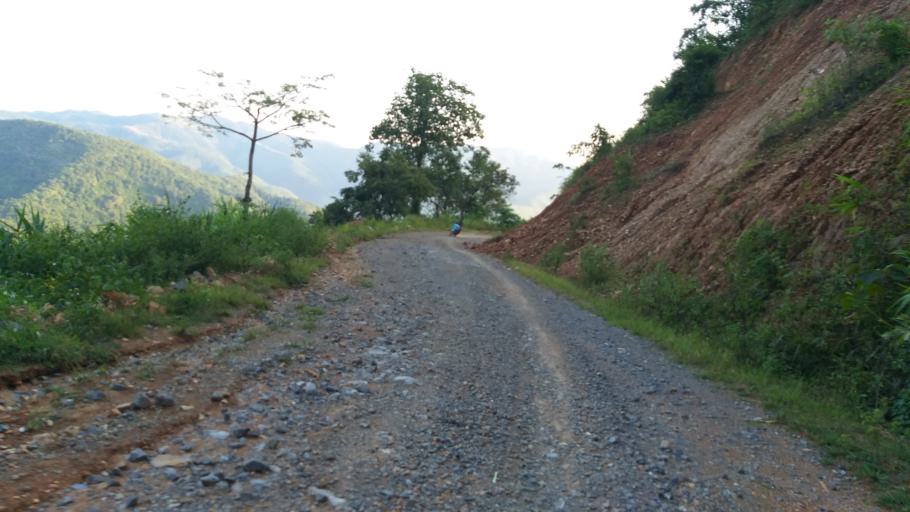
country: LA
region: Phongsali
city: Khoa
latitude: 21.1943
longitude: 102.5645
